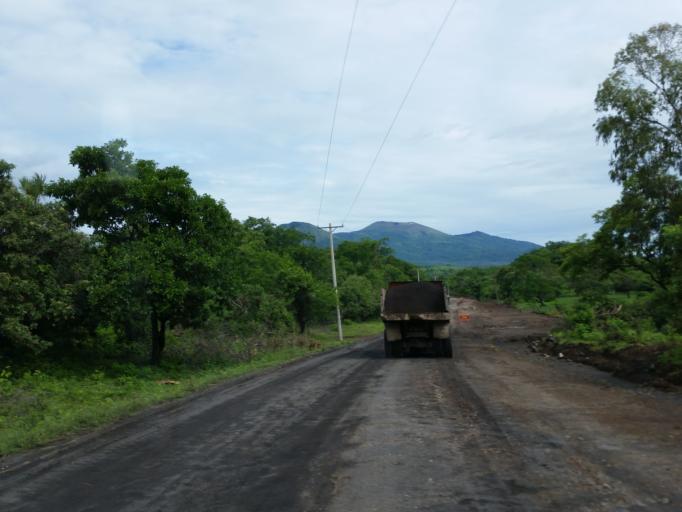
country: NI
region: Leon
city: La Paz Centro
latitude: 12.3790
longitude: -86.6621
